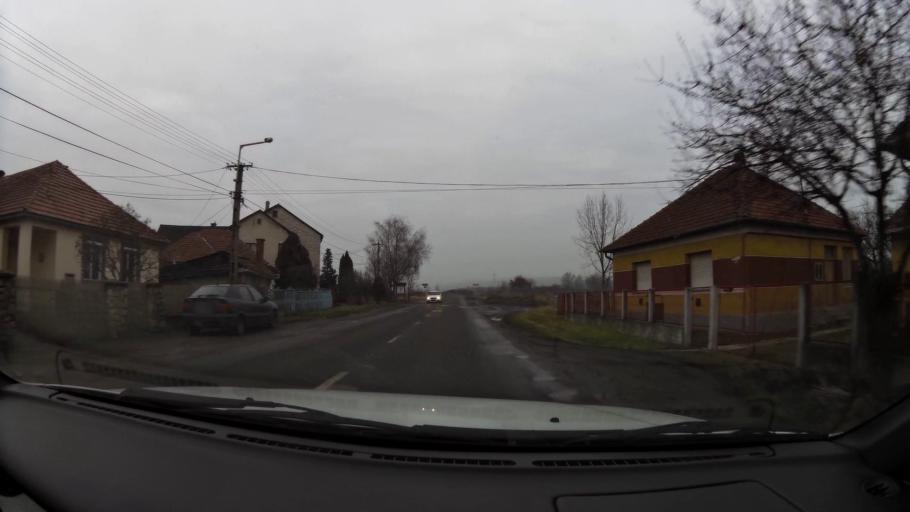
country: HU
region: Borsod-Abauj-Zemplen
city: Izsofalva
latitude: 48.2851
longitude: 20.6581
